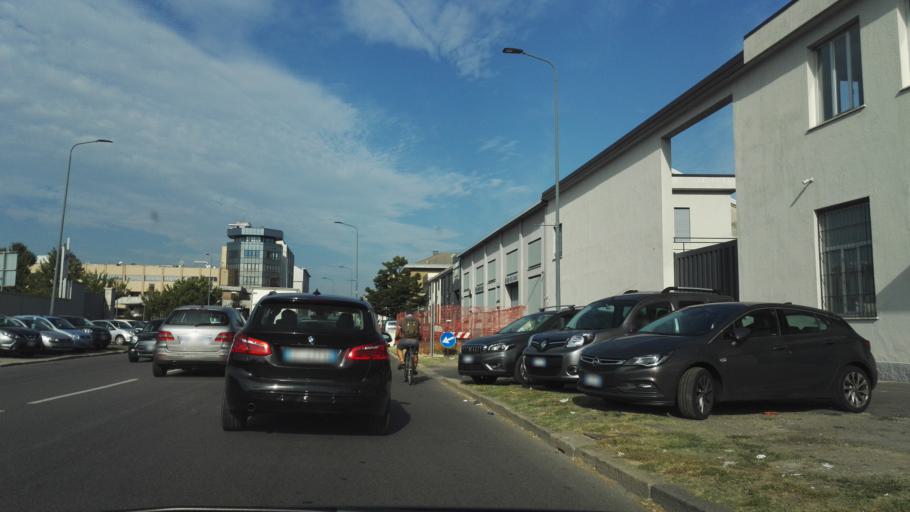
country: IT
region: Lombardy
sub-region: Citta metropolitana di Milano
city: Milano
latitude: 45.4397
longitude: 9.2050
